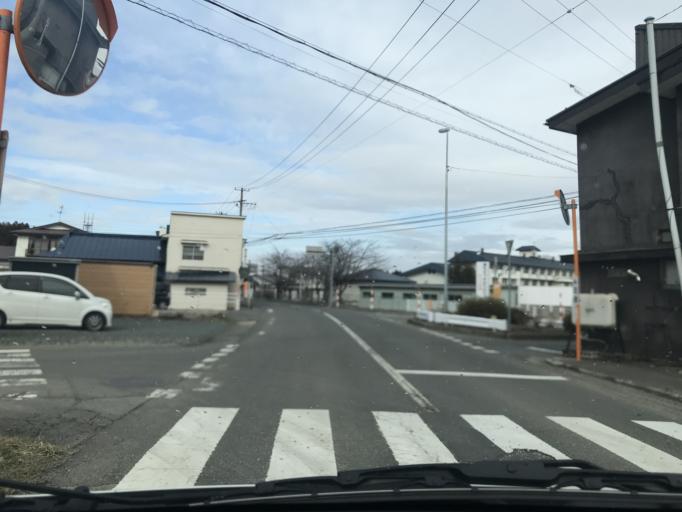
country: JP
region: Iwate
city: Hanamaki
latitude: 39.3458
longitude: 141.0462
